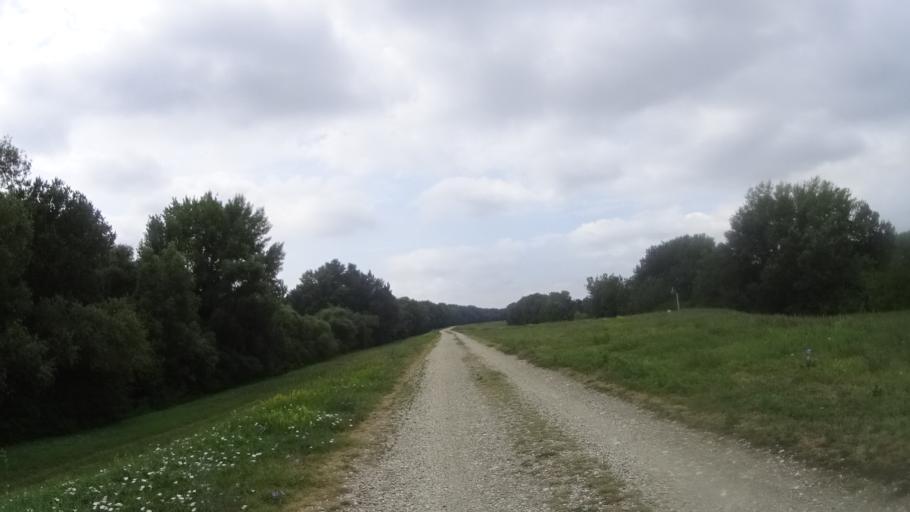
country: HU
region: Komarom-Esztergom
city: Acs
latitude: 47.7518
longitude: 17.9164
